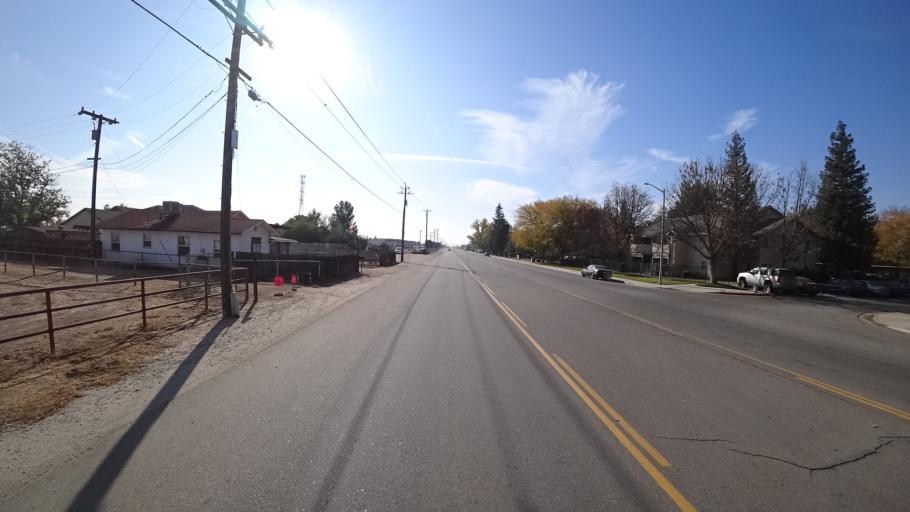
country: US
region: California
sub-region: Kern County
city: Greenacres
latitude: 35.3998
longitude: -119.0743
